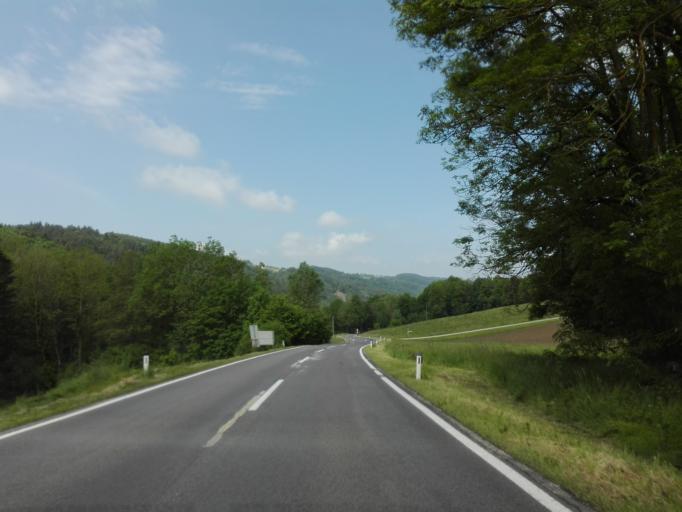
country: AT
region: Upper Austria
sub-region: Politischer Bezirk Rohrbach
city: Kleinzell im Muehlkreis
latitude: 48.3995
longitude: 13.9106
